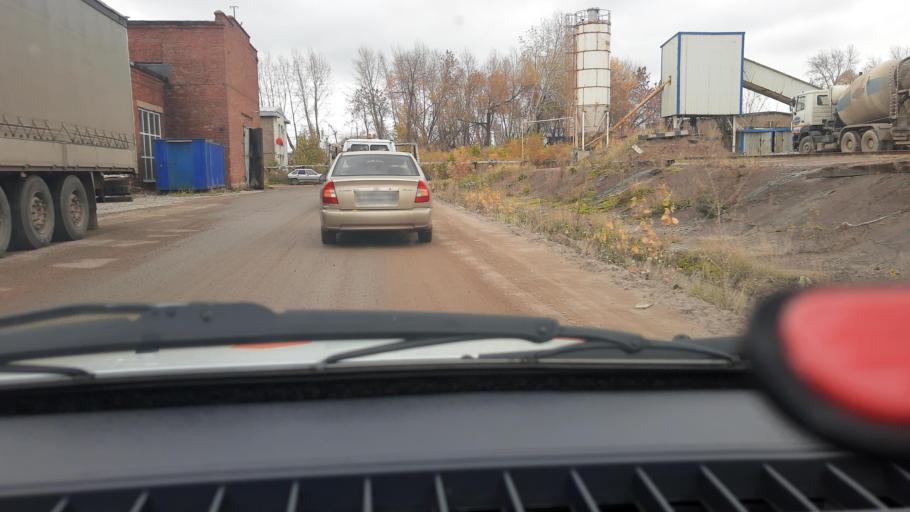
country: RU
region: Bashkortostan
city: Ufa
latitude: 54.8593
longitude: 56.1013
